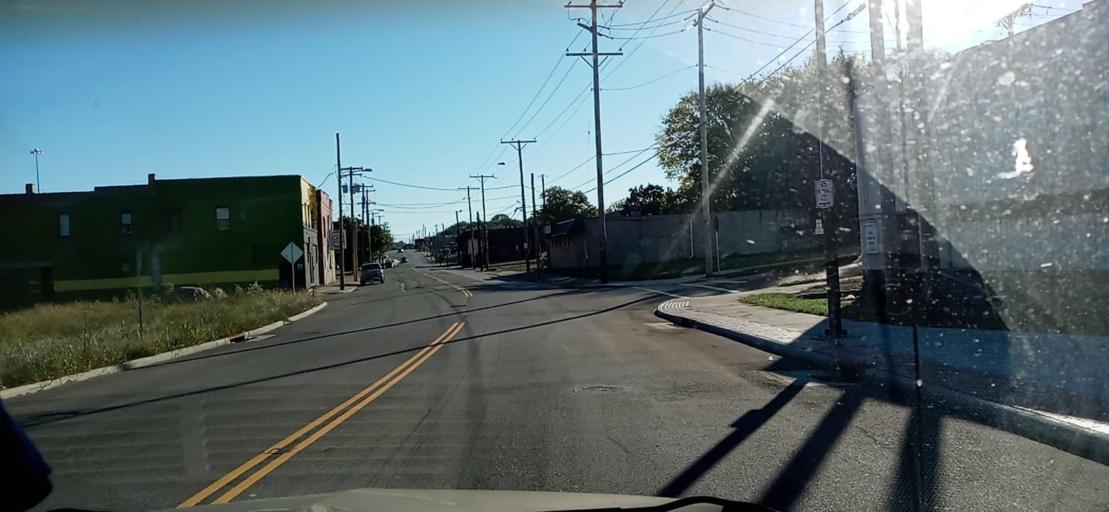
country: US
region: Ohio
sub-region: Summit County
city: Akron
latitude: 41.0604
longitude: -81.5237
